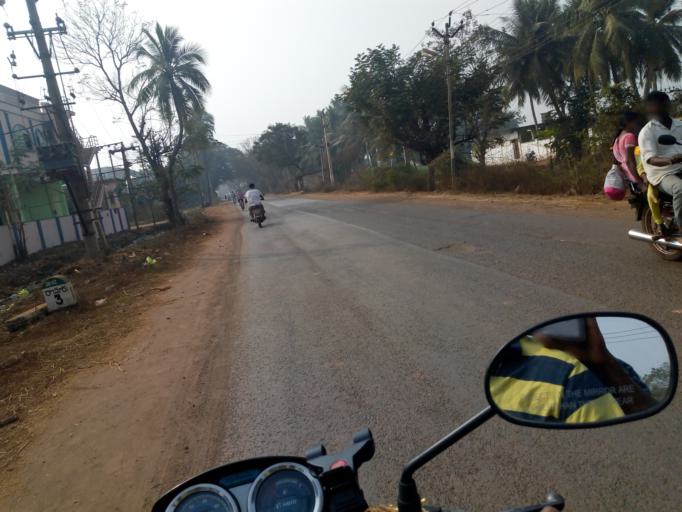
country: IN
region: Andhra Pradesh
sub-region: West Godavari
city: Tadepallegudem
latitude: 16.8136
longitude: 81.4082
